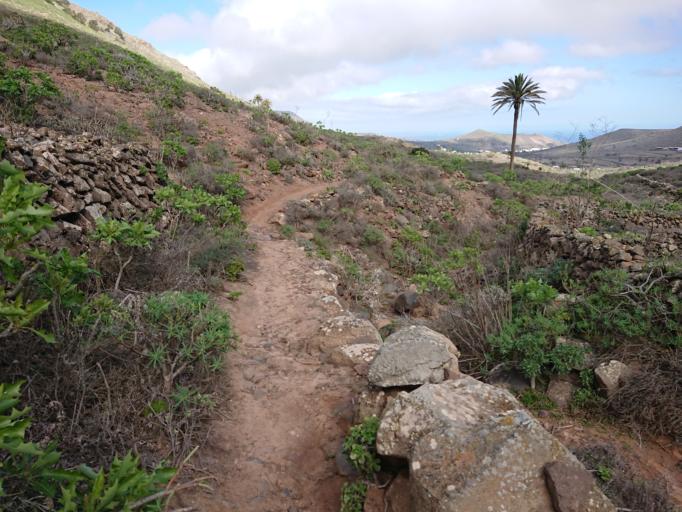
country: ES
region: Canary Islands
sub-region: Provincia de Las Palmas
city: Haria
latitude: 29.1333
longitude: -13.5171
